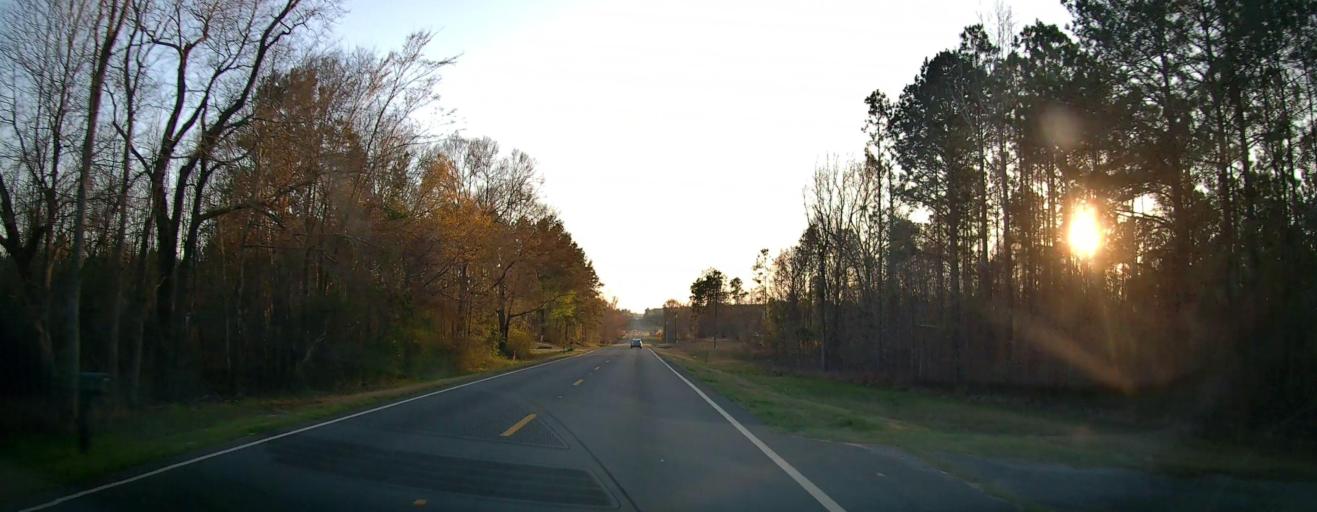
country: US
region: Georgia
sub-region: Laurens County
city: Dublin
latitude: 32.4077
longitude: -82.9640
